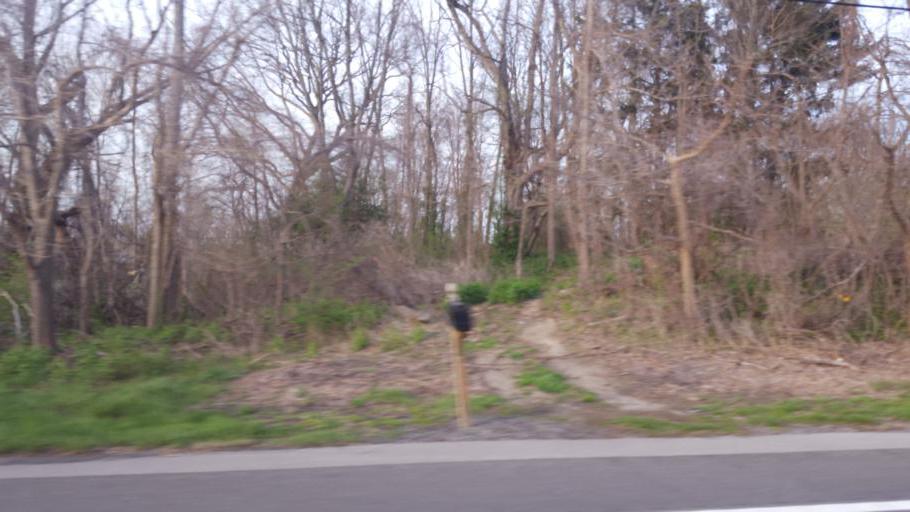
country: US
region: Ohio
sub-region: Erie County
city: Huron
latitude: 41.3837
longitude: -82.5166
